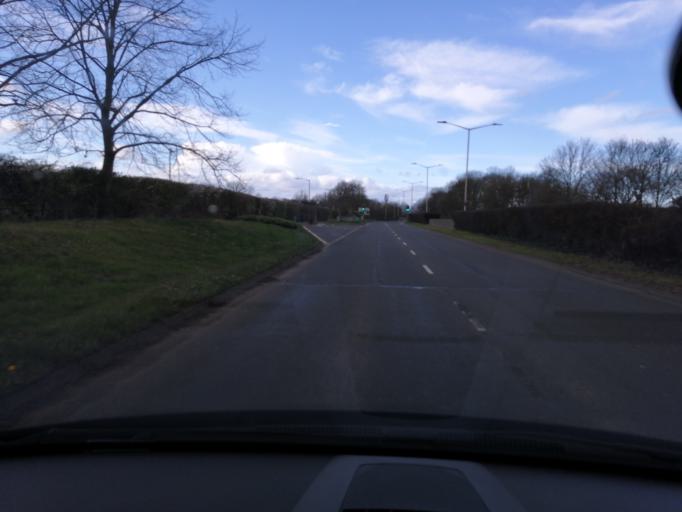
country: GB
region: England
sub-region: Peterborough
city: Peterborough
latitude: 52.5929
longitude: -0.2678
